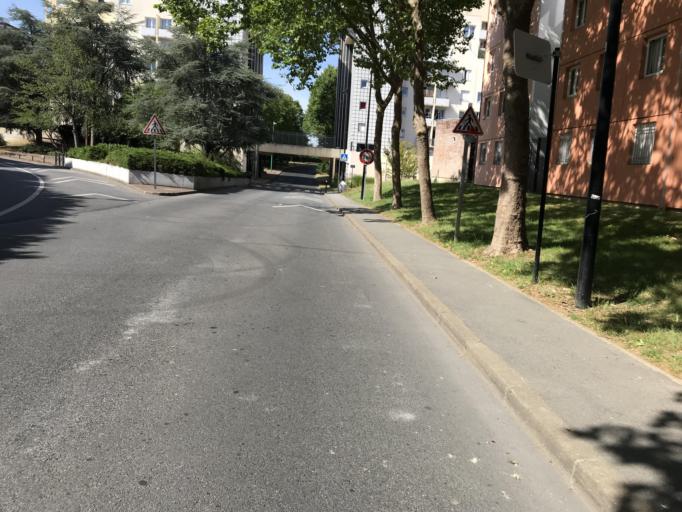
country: FR
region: Ile-de-France
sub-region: Departement de l'Essonne
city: Evry
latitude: 48.6358
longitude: 2.4297
